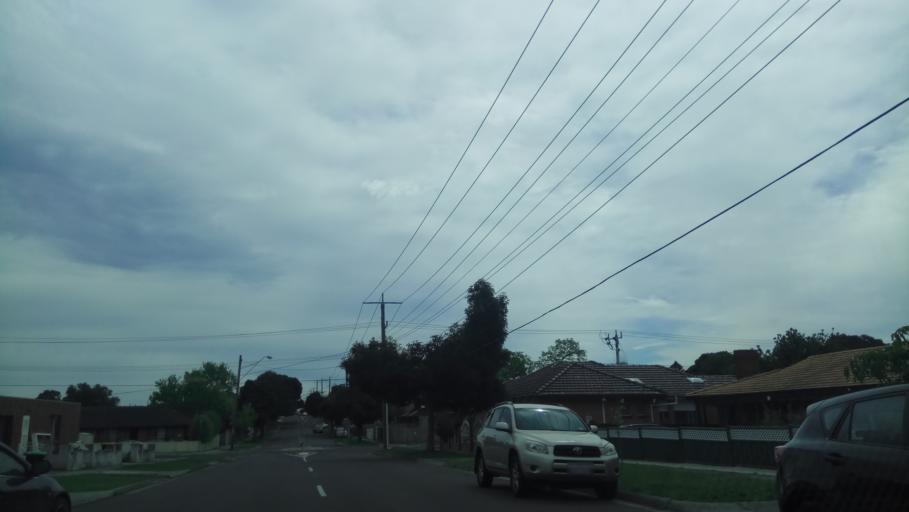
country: AU
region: Victoria
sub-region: Greater Dandenong
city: Springvale
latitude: -37.9540
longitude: 145.1430
